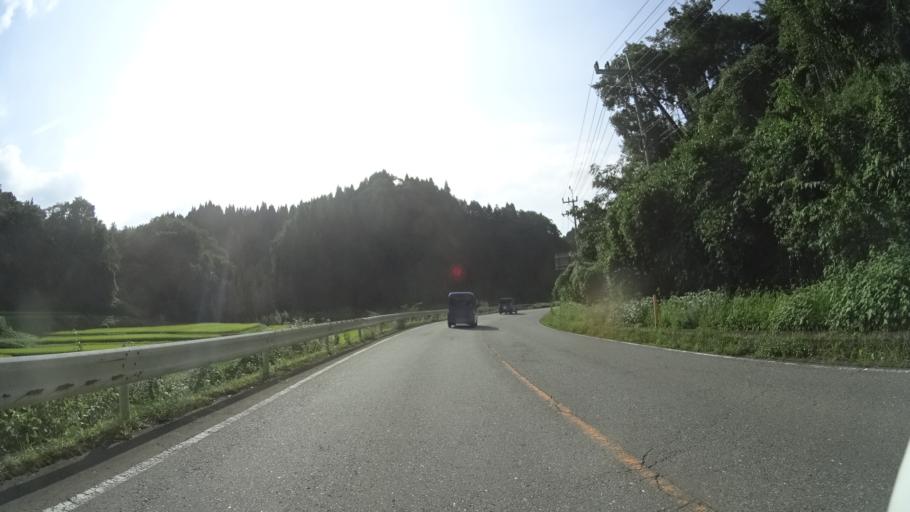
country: JP
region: Kumamoto
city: Aso
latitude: 32.6843
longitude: 131.0573
